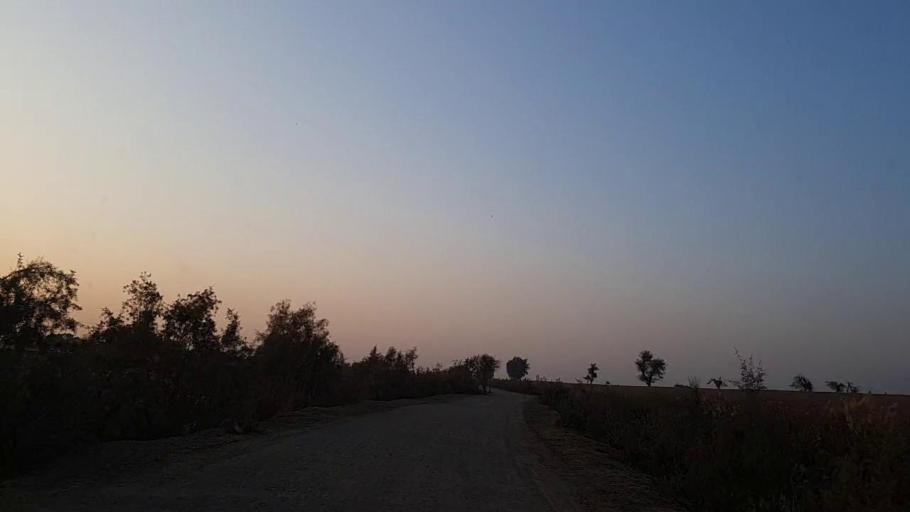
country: PK
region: Sindh
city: Bhit Shah
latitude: 25.9180
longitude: 68.4980
